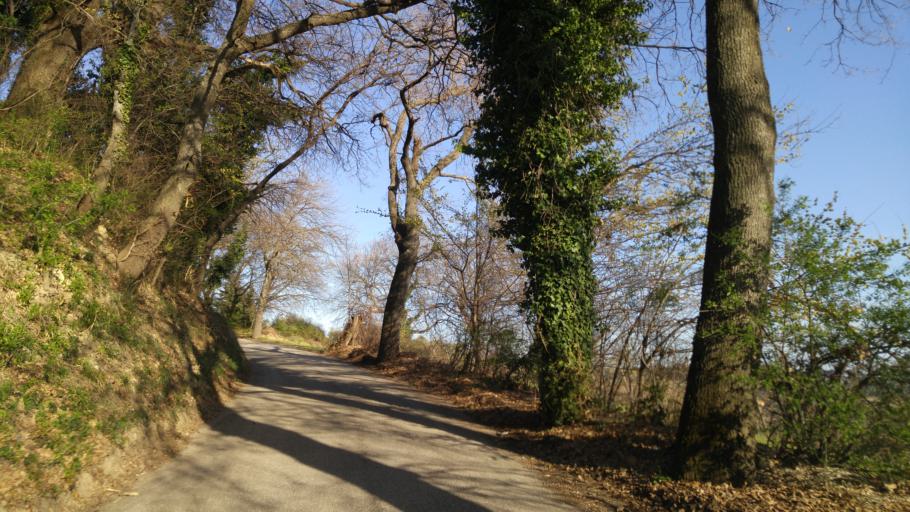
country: IT
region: The Marches
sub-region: Provincia di Pesaro e Urbino
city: Fenile
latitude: 43.8494
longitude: 12.9223
